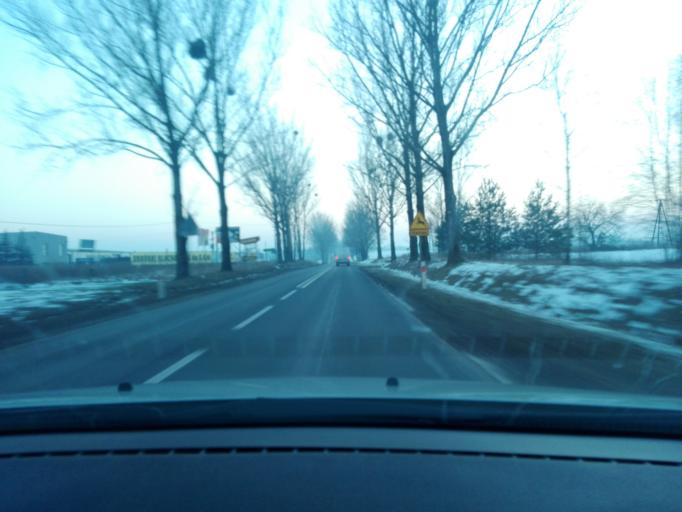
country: PL
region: Lodz Voivodeship
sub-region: Powiat zgierski
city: Zgierz
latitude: 51.9035
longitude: 19.4279
